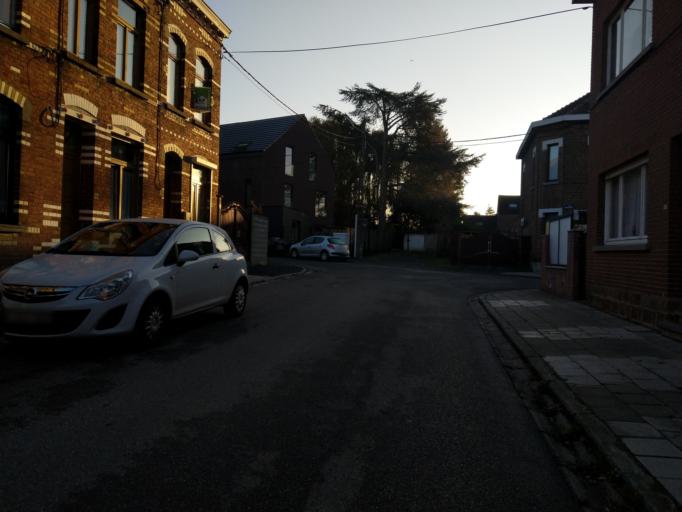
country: BE
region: Wallonia
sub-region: Province du Hainaut
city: Mons
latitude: 50.4666
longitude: 3.9598
